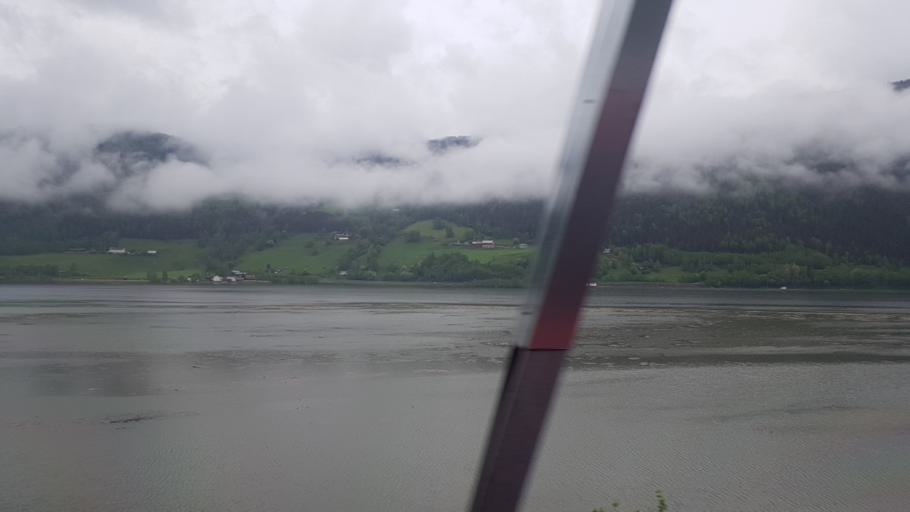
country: NO
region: Oppland
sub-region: Ringebu
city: Ringebu
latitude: 61.4326
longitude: 10.1834
